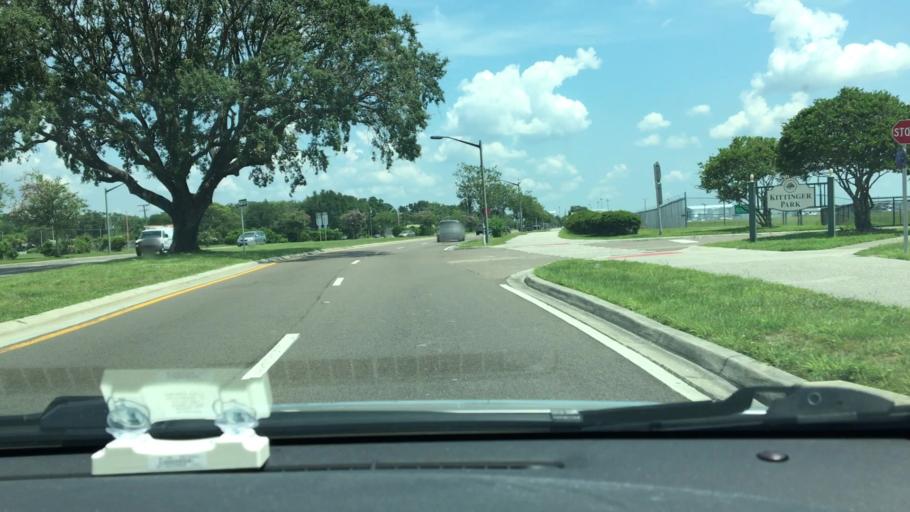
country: US
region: Florida
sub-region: Orange County
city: Orlando
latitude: 28.5391
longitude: -81.3436
